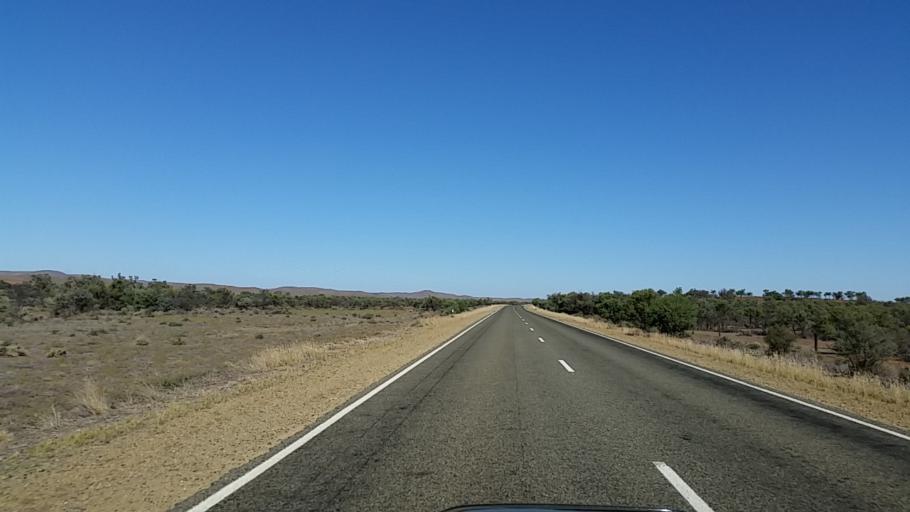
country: AU
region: South Australia
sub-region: Flinders Ranges
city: Quorn
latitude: -32.3921
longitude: 138.5079
